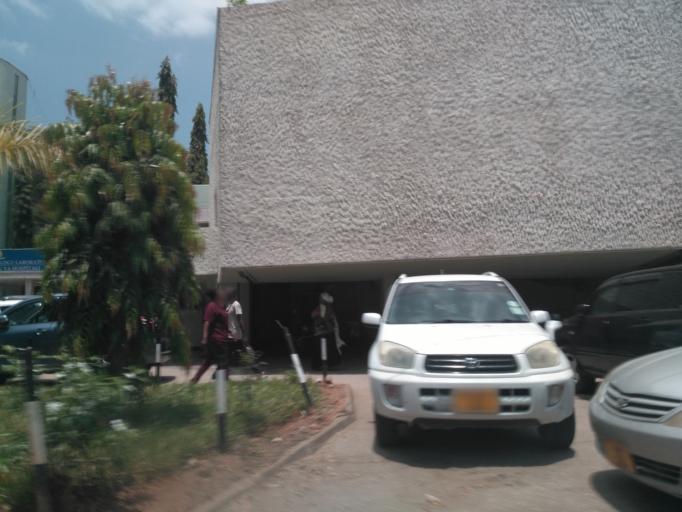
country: TZ
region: Dar es Salaam
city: Dar es Salaam
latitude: -6.8037
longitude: 39.2731
